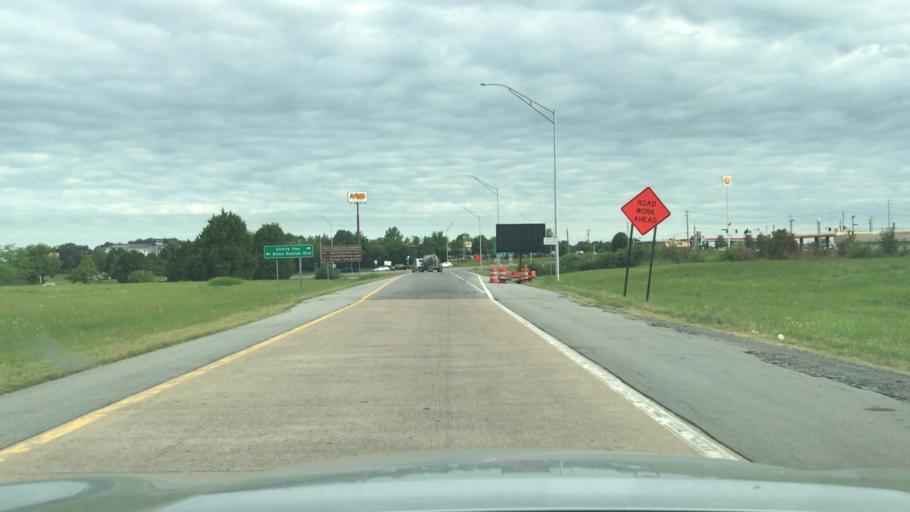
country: US
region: Tennessee
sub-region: Montgomery County
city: Clarksville
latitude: 36.5995
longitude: -87.2801
